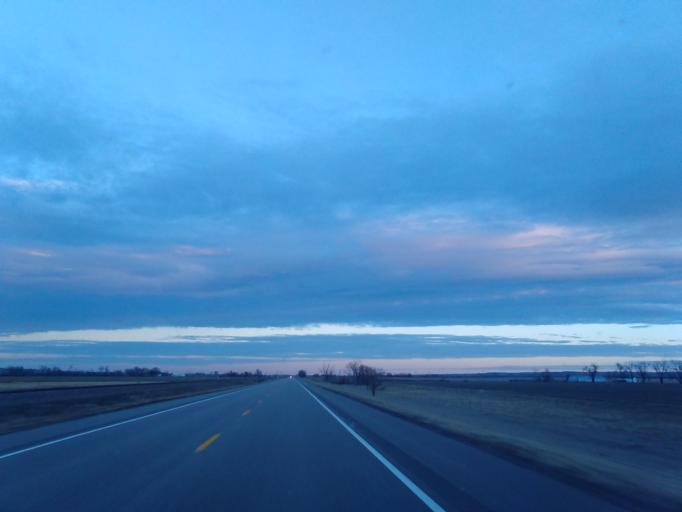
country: US
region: Nebraska
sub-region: Garden County
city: Oshkosh
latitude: 41.3986
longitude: -102.3229
